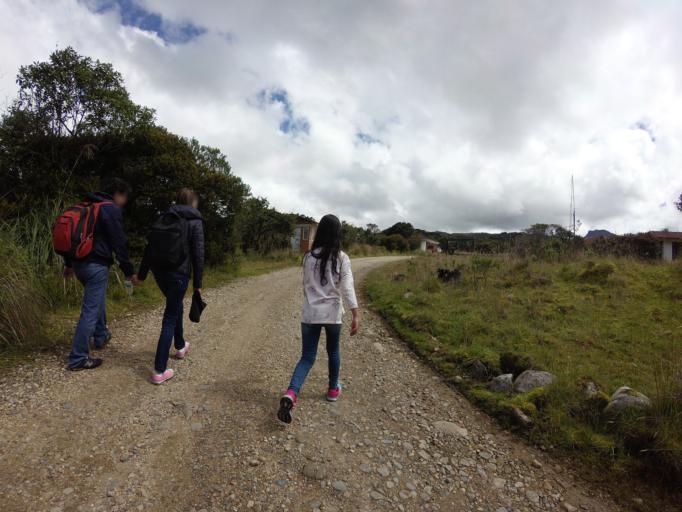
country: CO
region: Cundinamarca
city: Junin
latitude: 4.6290
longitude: -73.7238
